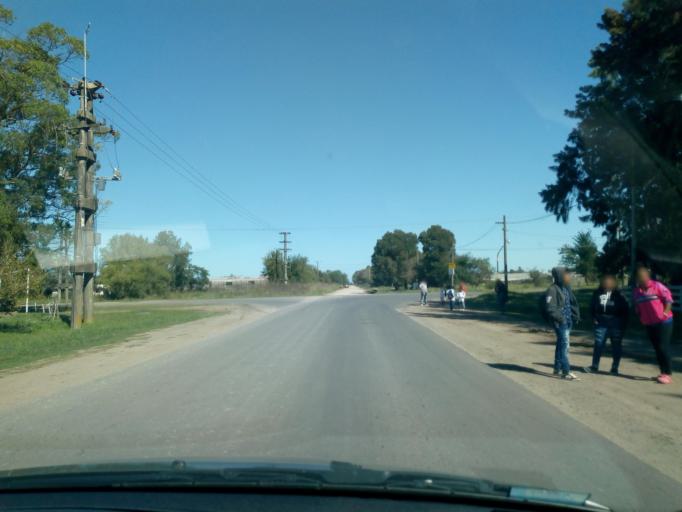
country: AR
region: Buenos Aires
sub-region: Partido de La Plata
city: La Plata
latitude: -35.0102
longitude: -58.0273
